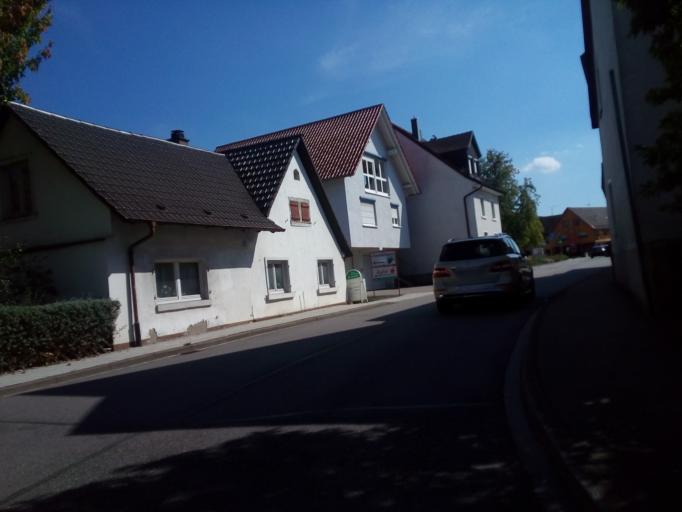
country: DE
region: Baden-Wuerttemberg
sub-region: Freiburg Region
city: Achern
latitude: 48.6194
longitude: 8.0831
